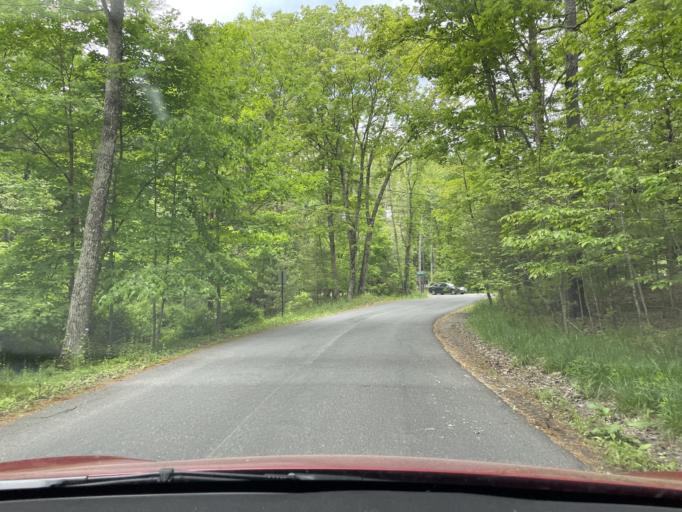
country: US
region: New York
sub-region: Ulster County
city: West Hurley
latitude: 42.0190
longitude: -74.0988
